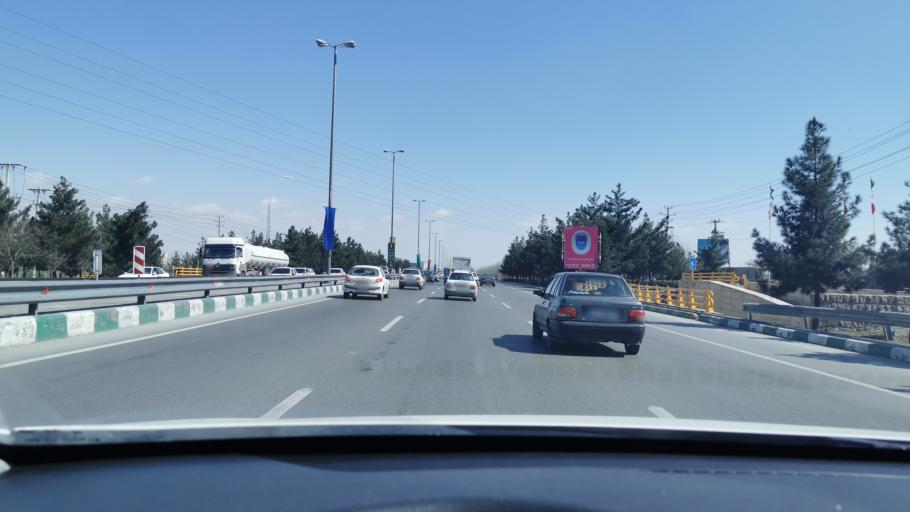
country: IR
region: Razavi Khorasan
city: Mashhad
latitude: 36.2726
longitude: 59.5633
